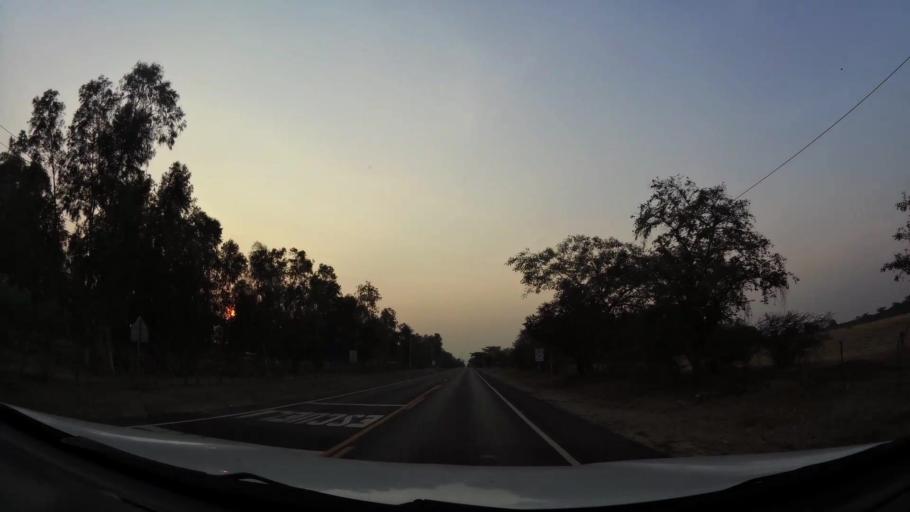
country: NI
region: Leon
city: La Paz Centro
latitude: 12.3258
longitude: -86.8003
